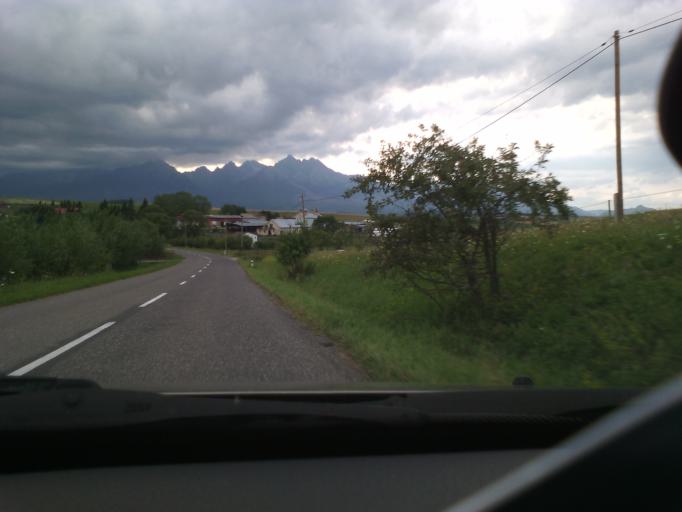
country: SK
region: Presovsky
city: Lubica
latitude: 49.0848
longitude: 20.4070
